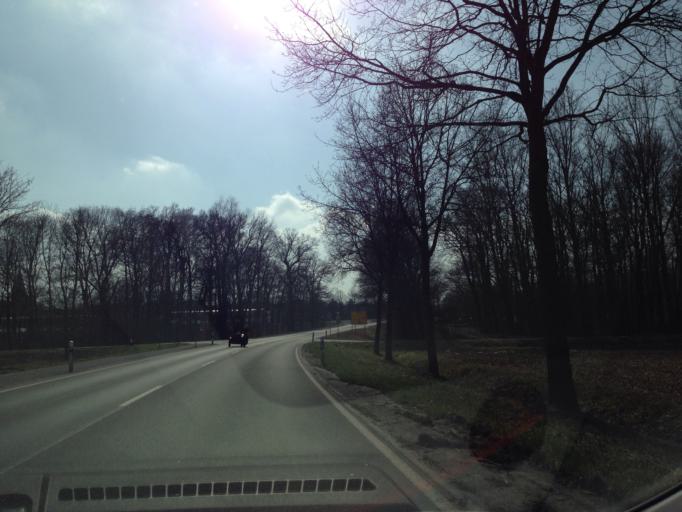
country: DE
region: North Rhine-Westphalia
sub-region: Regierungsbezirk Munster
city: Muenster
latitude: 52.0025
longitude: 7.5574
